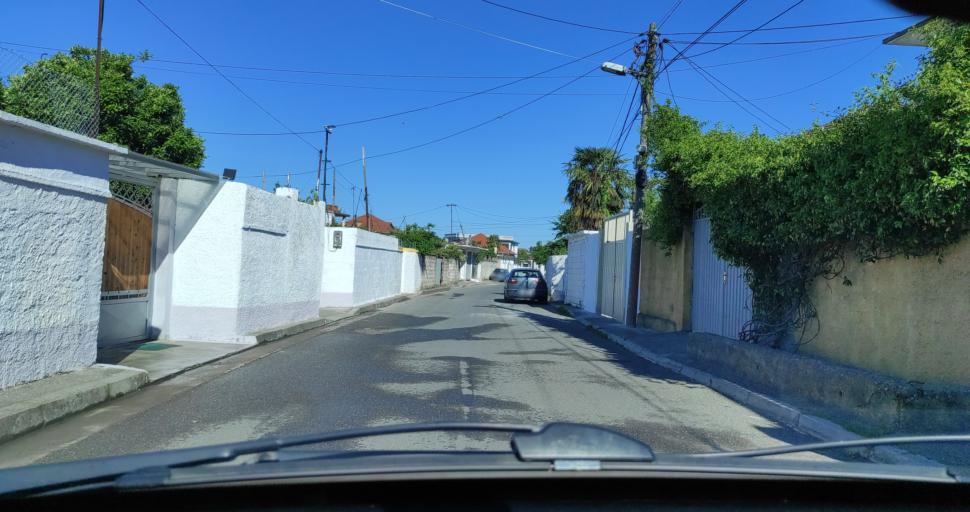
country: AL
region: Shkoder
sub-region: Rrethi i Shkodres
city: Shkoder
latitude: 42.0784
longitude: 19.5049
